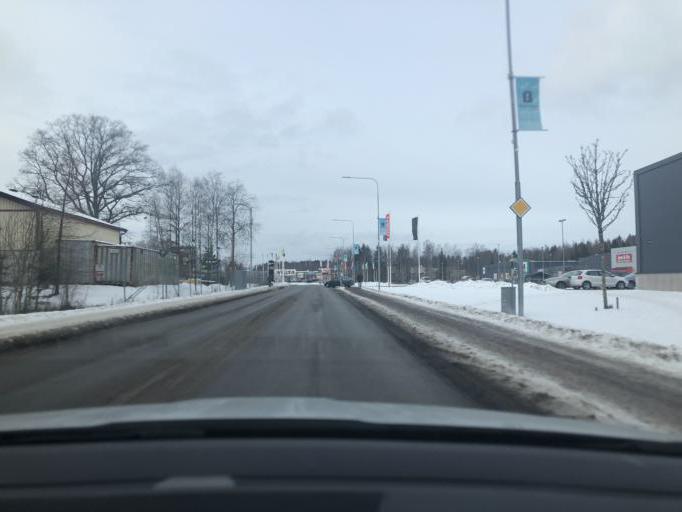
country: SE
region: OEstergoetland
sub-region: Motala Kommun
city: Motala
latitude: 58.5571
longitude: 15.0414
